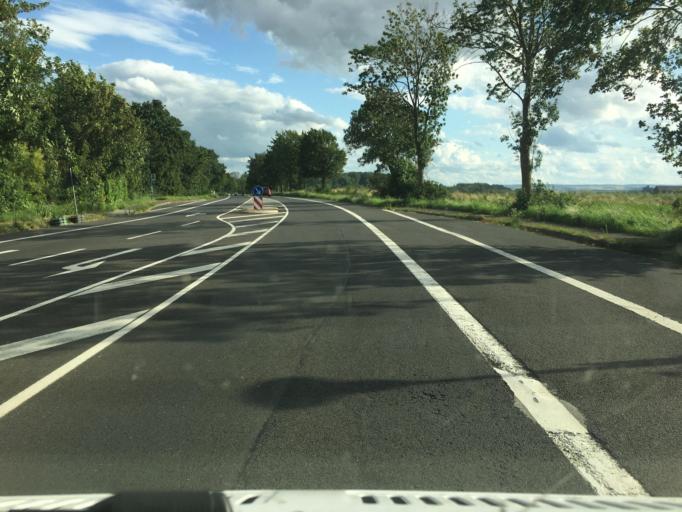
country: DE
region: North Rhine-Westphalia
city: Zulpich
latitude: 50.7296
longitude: 6.6623
